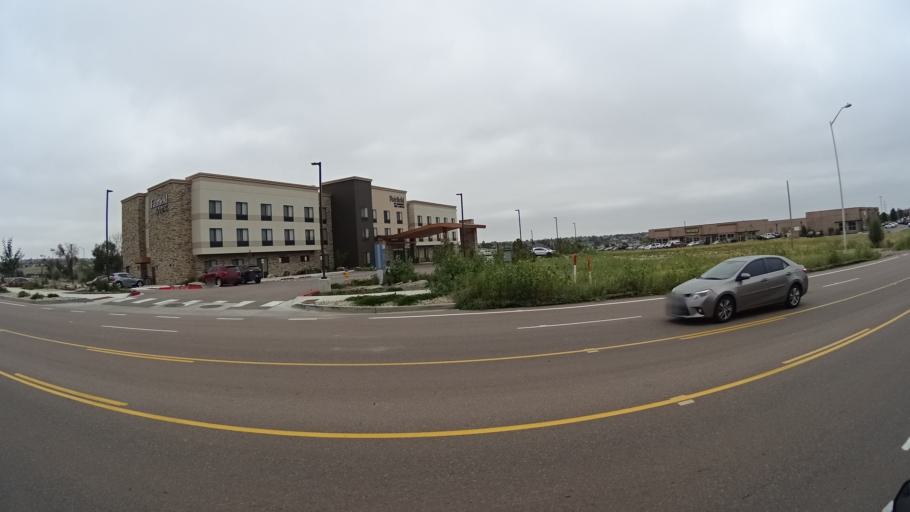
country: US
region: Colorado
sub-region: El Paso County
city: Cimarron Hills
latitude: 38.8915
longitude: -104.7148
